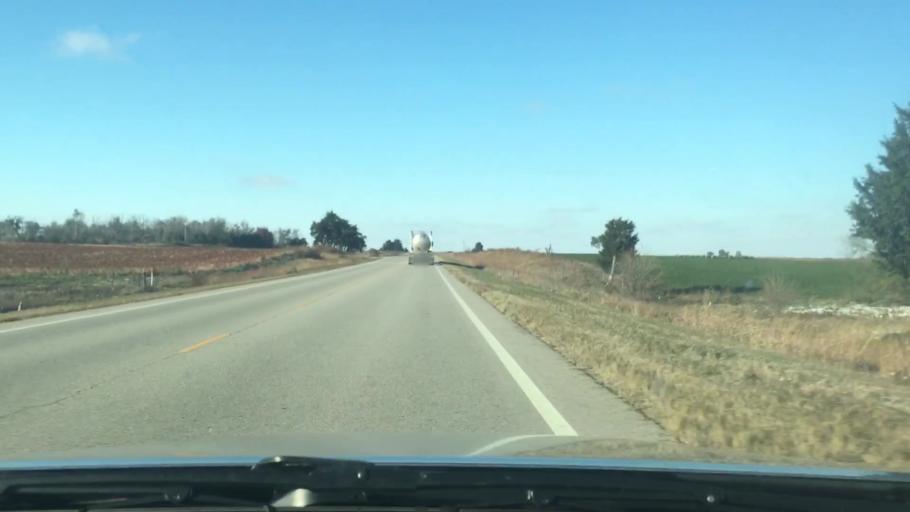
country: US
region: Kansas
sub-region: Rice County
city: Sterling
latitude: 38.1502
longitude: -98.2042
